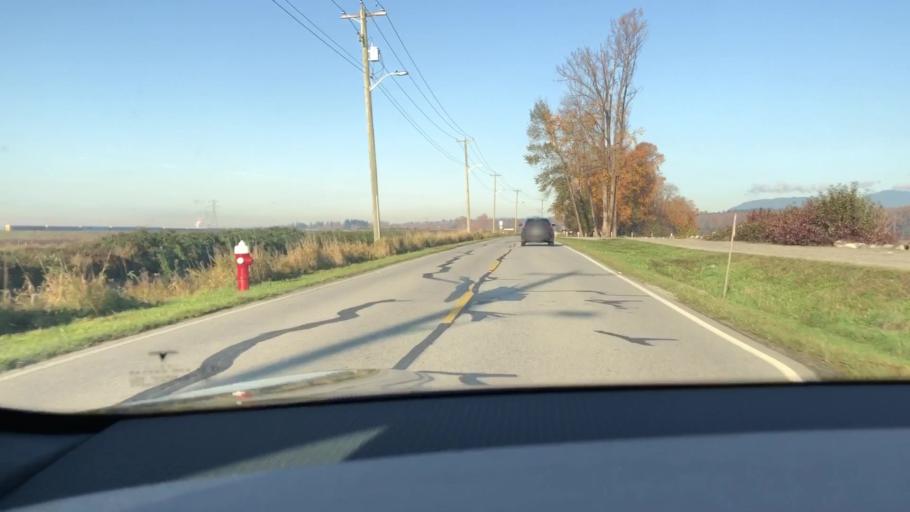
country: CA
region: British Columbia
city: New Westminster
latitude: 49.1860
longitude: -122.9968
